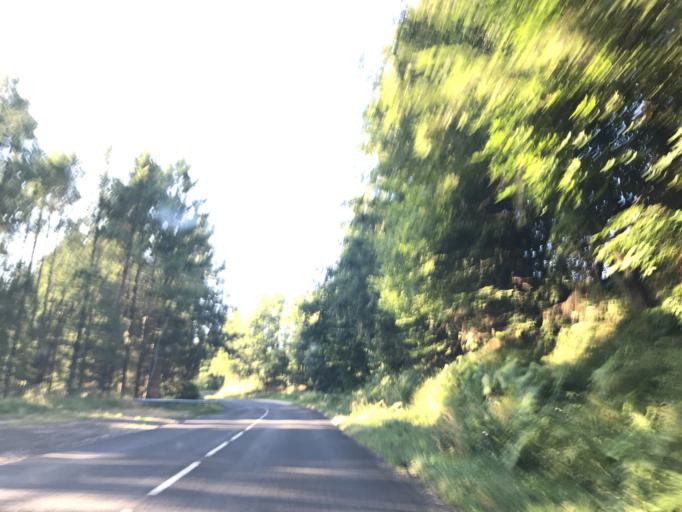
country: FR
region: Auvergne
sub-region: Departement du Puy-de-Dome
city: La Monnerie-le-Montel
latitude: 45.8784
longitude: 3.5999
